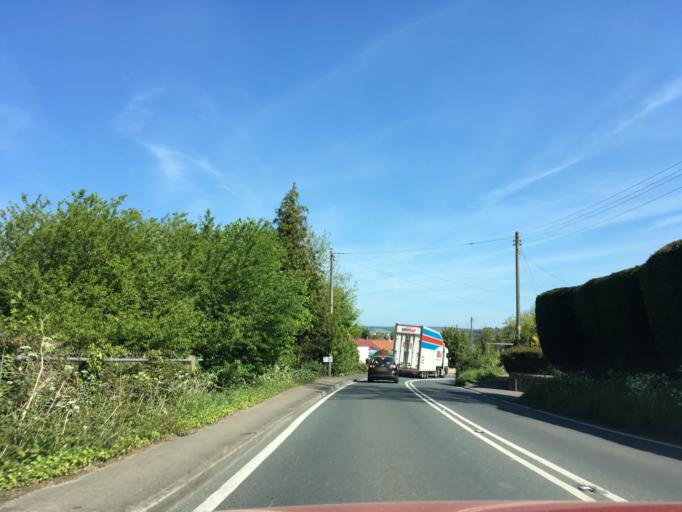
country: GB
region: England
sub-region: Gloucestershire
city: Nailsworth
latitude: 51.6855
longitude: -2.2231
